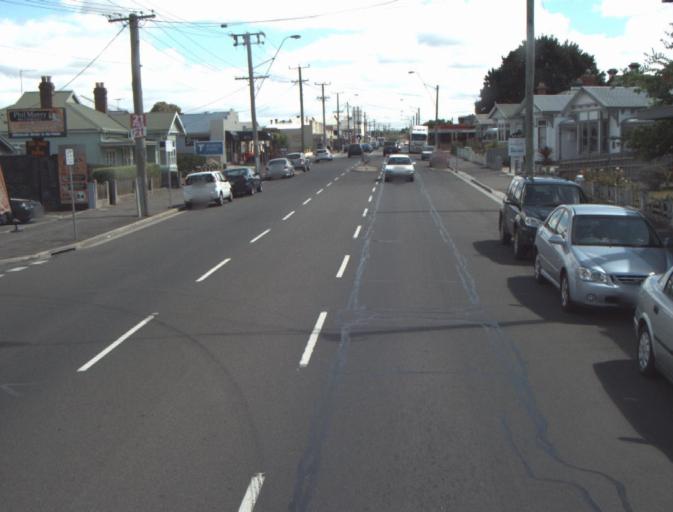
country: AU
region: Tasmania
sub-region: Launceston
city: Launceston
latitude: -41.4210
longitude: 147.1355
